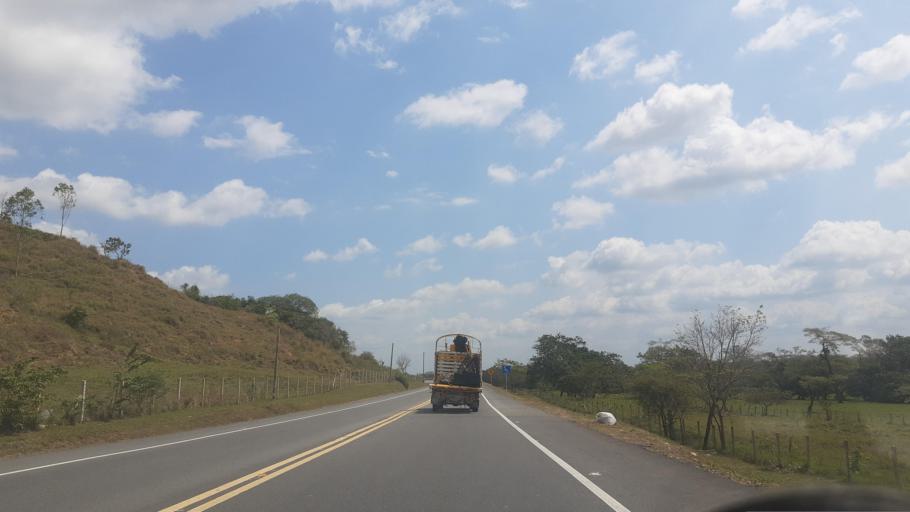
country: CO
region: Casanare
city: Tauramena
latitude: 5.0184
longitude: -72.6699
